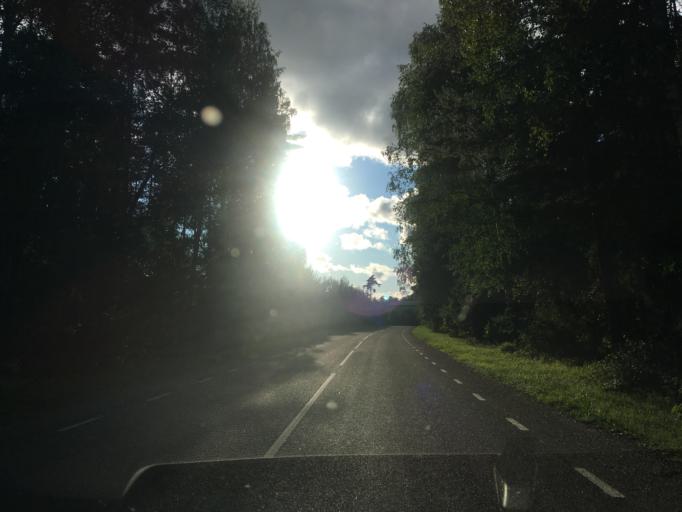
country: EE
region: Raplamaa
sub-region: Maerjamaa vald
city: Marjamaa
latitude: 58.8978
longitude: 24.4471
